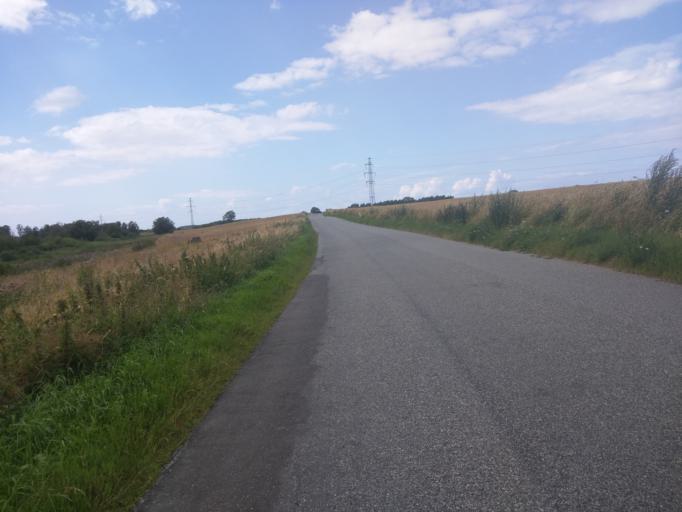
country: DK
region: Zealand
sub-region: Kalundborg Kommune
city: Svebolle
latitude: 55.6865
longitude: 11.2992
